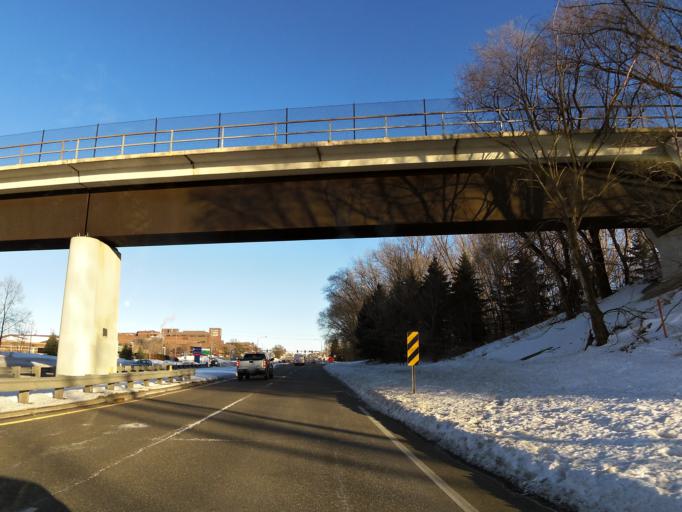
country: US
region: Minnesota
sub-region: Ramsey County
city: Vadnais Heights
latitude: 45.0280
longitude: -93.0388
